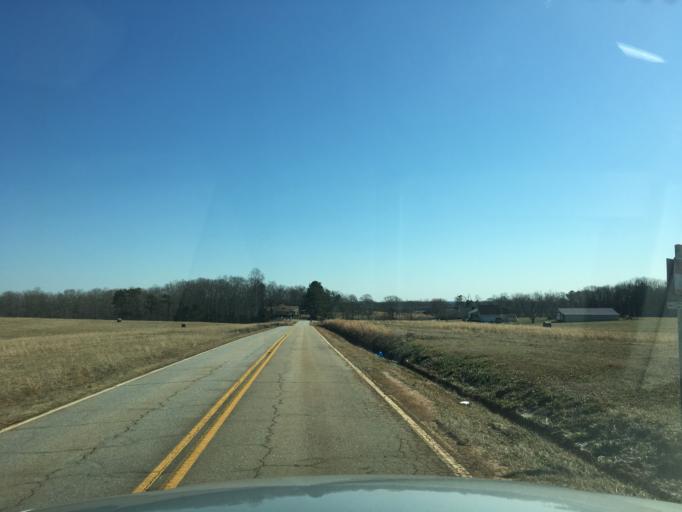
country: US
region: South Carolina
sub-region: Pickens County
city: Liberty
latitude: 34.8184
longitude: -82.7752
